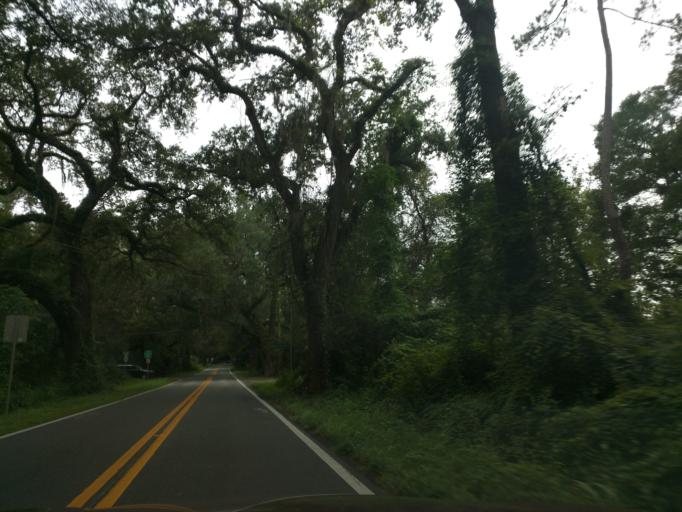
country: US
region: Florida
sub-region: Leon County
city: Tallahassee
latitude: 30.4843
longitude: -84.1984
